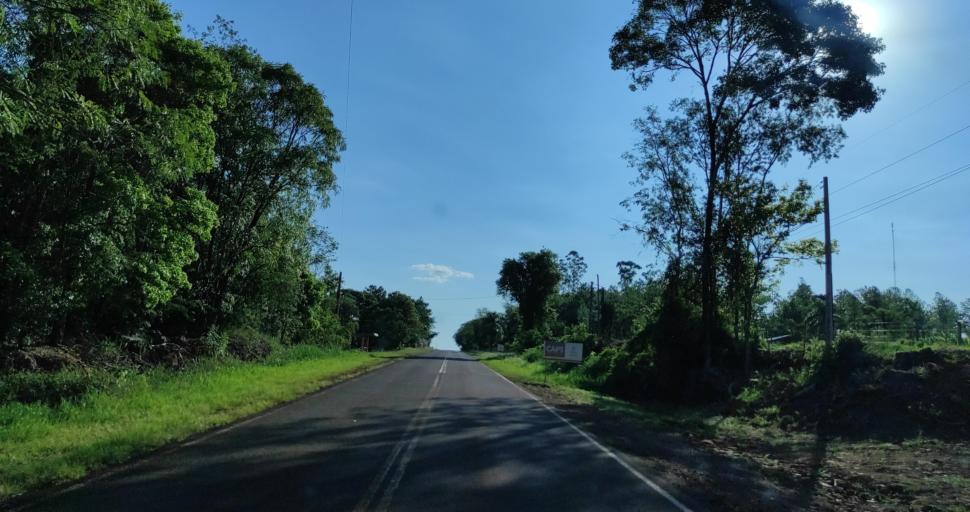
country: AR
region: Misiones
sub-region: Departamento de Eldorado
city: Eldorado
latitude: -26.3887
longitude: -54.3548
